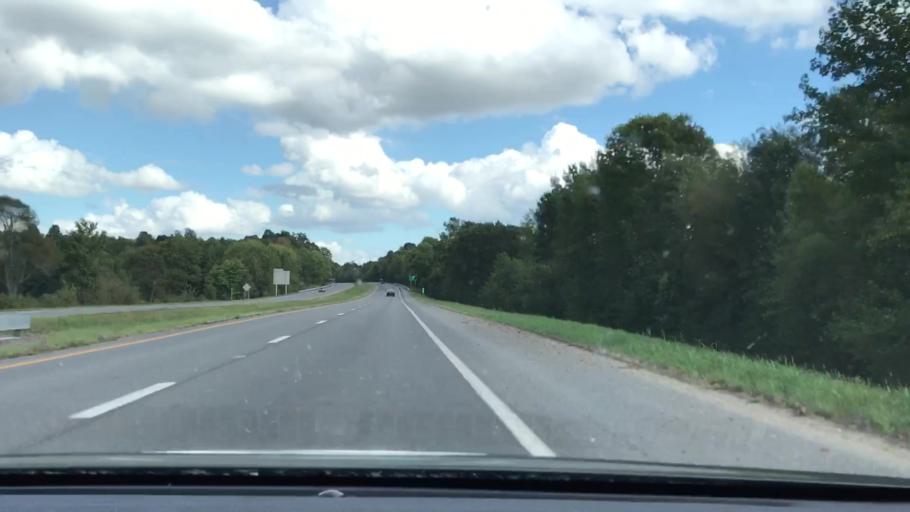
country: US
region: Kentucky
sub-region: Graves County
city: Mayfield
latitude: 36.7694
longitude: -88.6224
